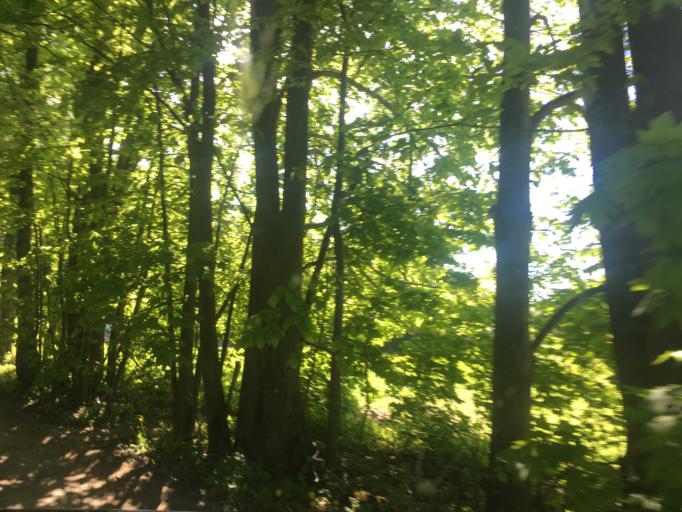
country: PL
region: Warmian-Masurian Voivodeship
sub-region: Powiat piski
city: Ruciane-Nida
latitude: 53.6556
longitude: 21.4833
